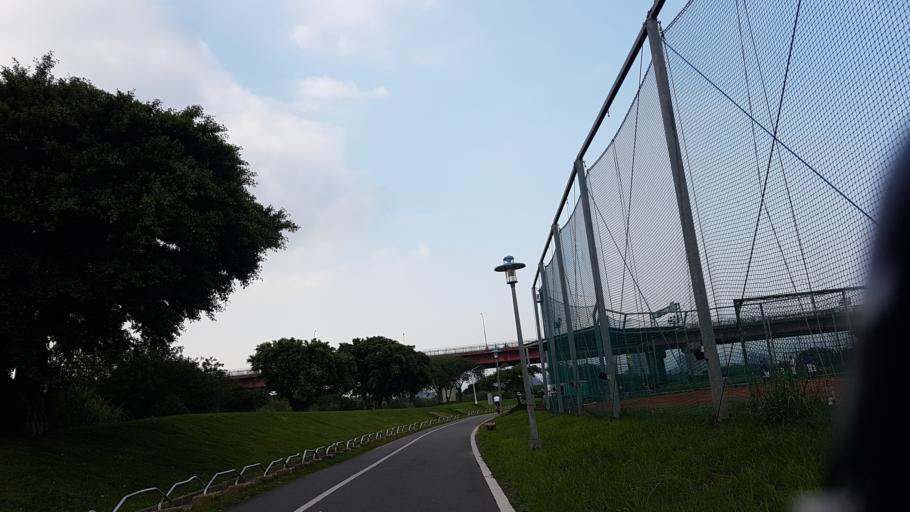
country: TW
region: Taipei
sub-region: Taipei
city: Banqiao
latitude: 25.0340
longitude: 121.4864
